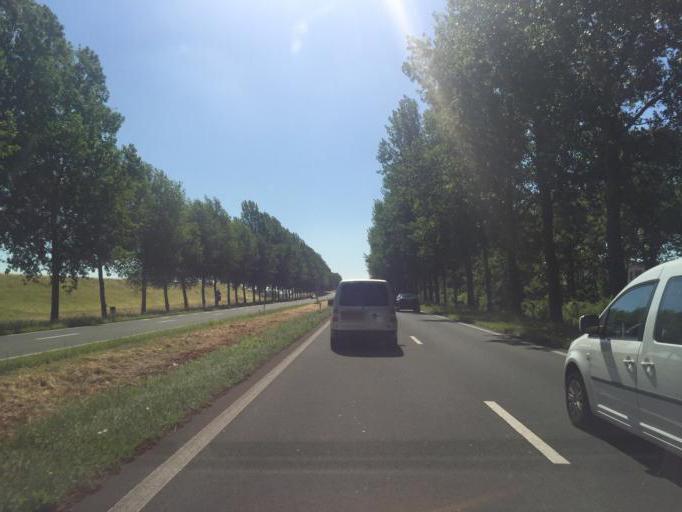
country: NL
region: North Holland
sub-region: Gemeente Haarlemmermeer
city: Hoofddorp
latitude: 52.3166
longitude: 4.6943
